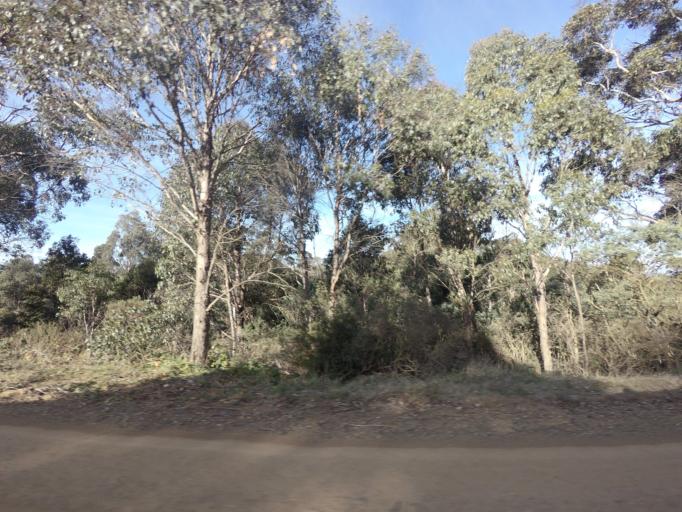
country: AU
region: Tasmania
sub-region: Brighton
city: Bridgewater
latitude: -42.4872
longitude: 147.3855
